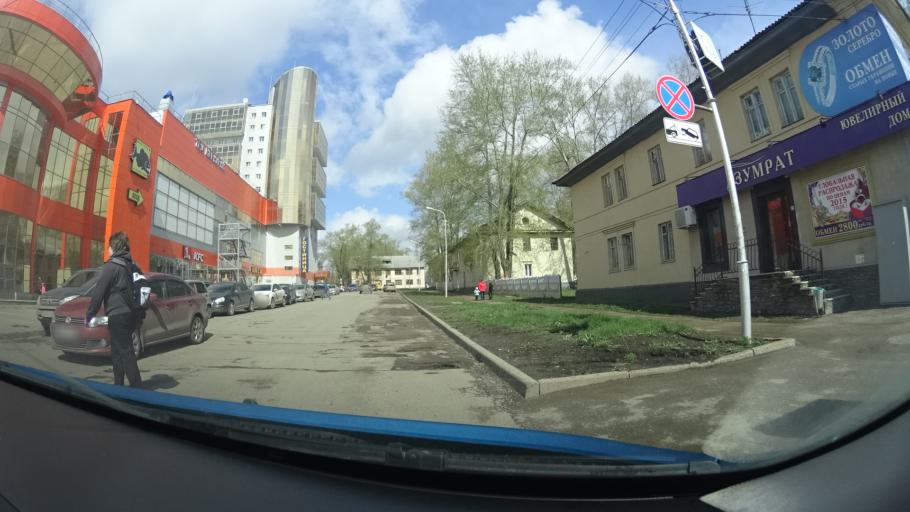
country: RU
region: Bashkortostan
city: Ufa
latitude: 54.8218
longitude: 56.0865
